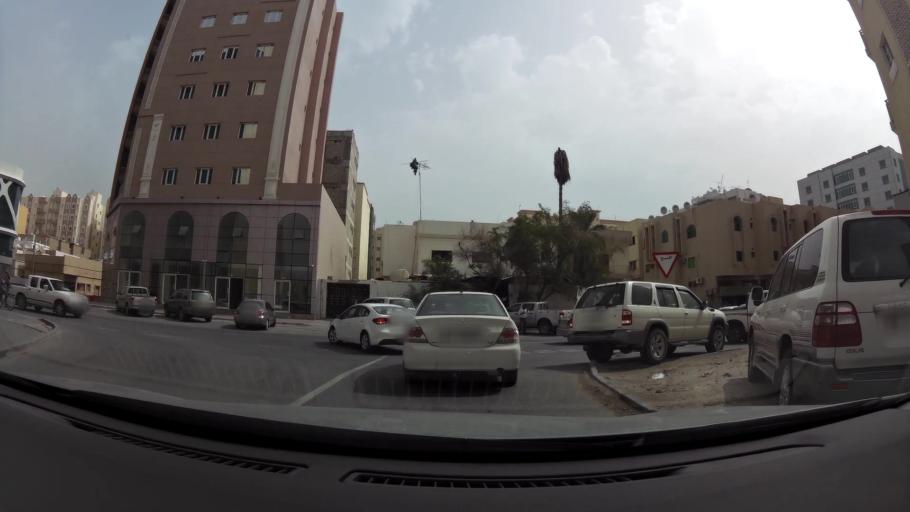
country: QA
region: Baladiyat ad Dawhah
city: Doha
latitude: 25.2672
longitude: 51.5448
